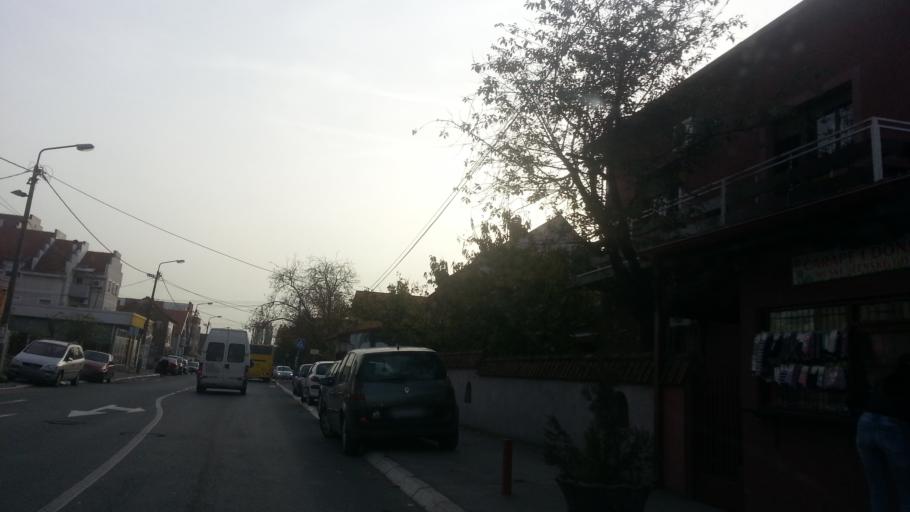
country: RS
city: Novi Banovci
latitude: 44.8975
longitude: 20.2905
